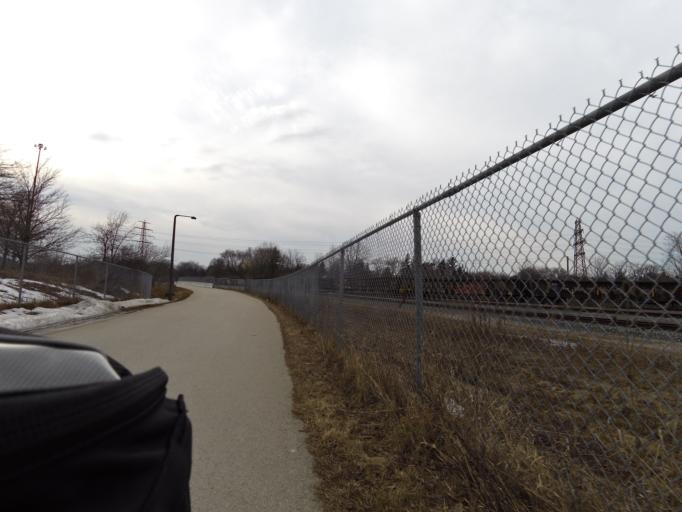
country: CA
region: Ontario
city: Hamilton
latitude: 43.2528
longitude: -79.9135
